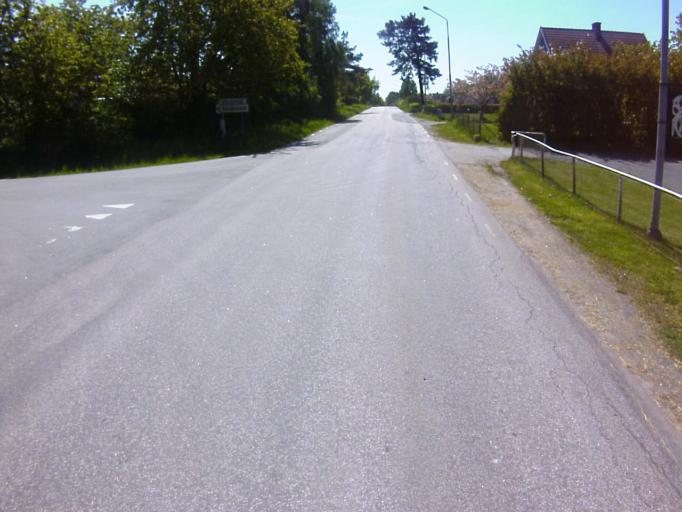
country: SE
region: Blekinge
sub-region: Solvesborgs Kommun
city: Soelvesborg
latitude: 56.0557
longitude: 14.6223
